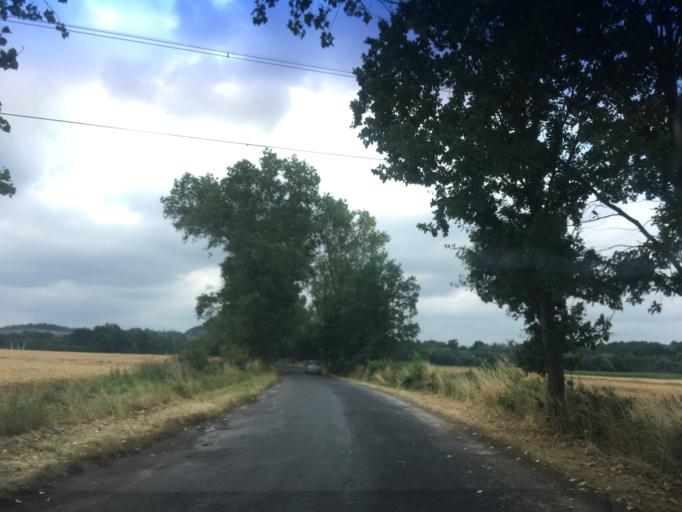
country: PL
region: Lower Silesian Voivodeship
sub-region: Powiat zgorzelecki
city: Sulikow
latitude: 51.0899
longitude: 15.0652
